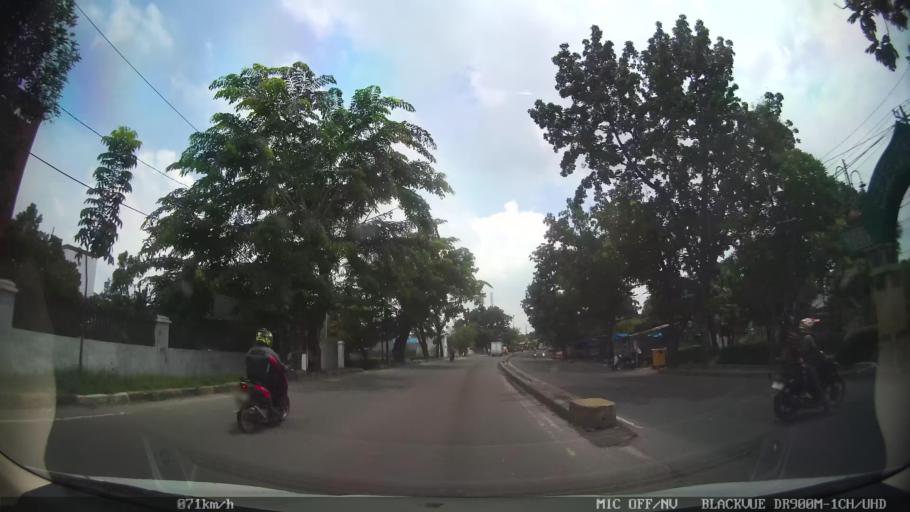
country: ID
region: North Sumatra
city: Labuhan Deli
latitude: 3.6614
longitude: 98.6664
